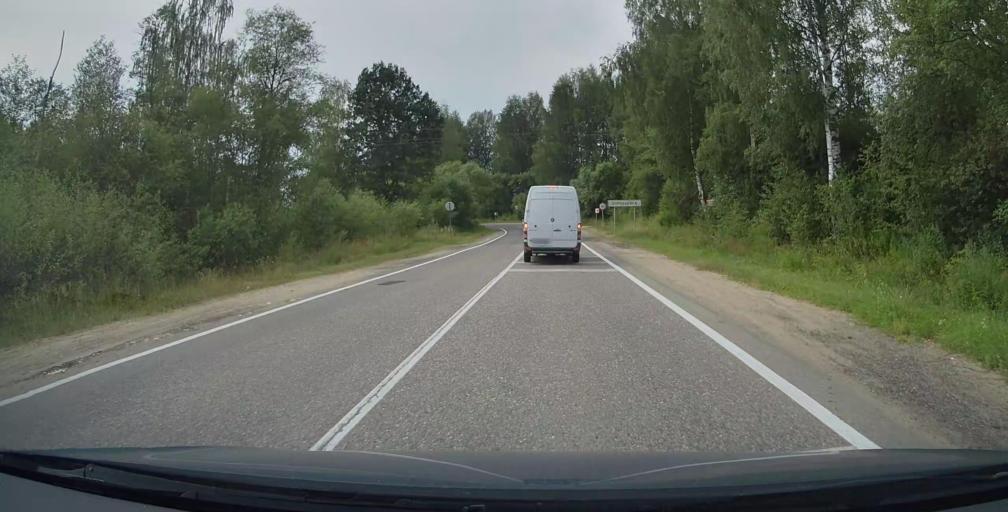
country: RU
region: Jaroslavl
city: Rybinsk
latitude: 57.9774
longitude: 38.7419
